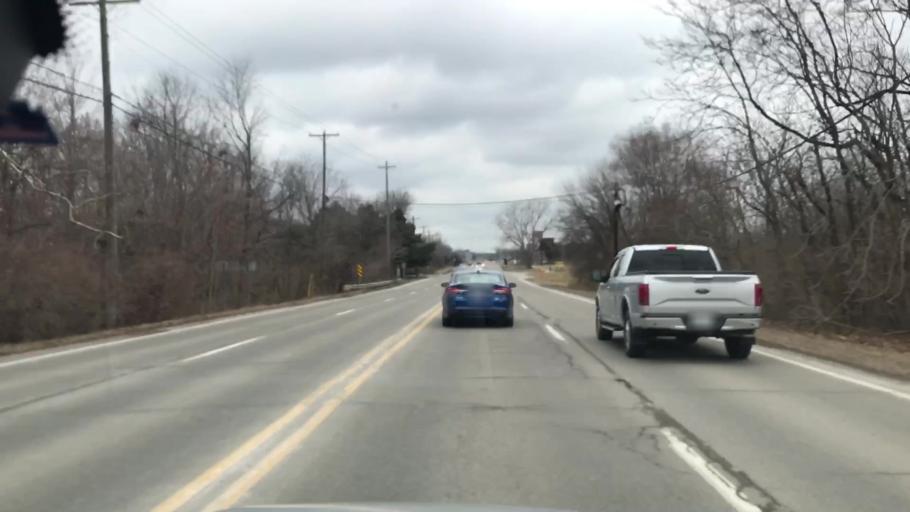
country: US
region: Michigan
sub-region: Wayne County
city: Plymouth
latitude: 42.3721
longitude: -83.4322
